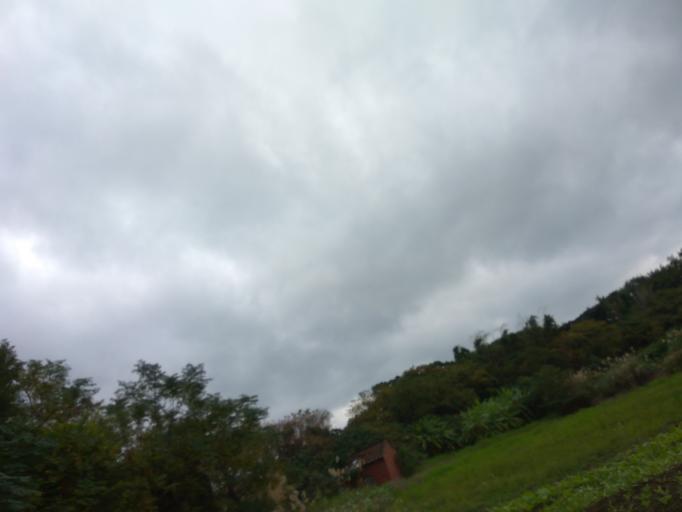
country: TW
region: Taiwan
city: Taoyuan City
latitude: 25.0261
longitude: 121.2238
